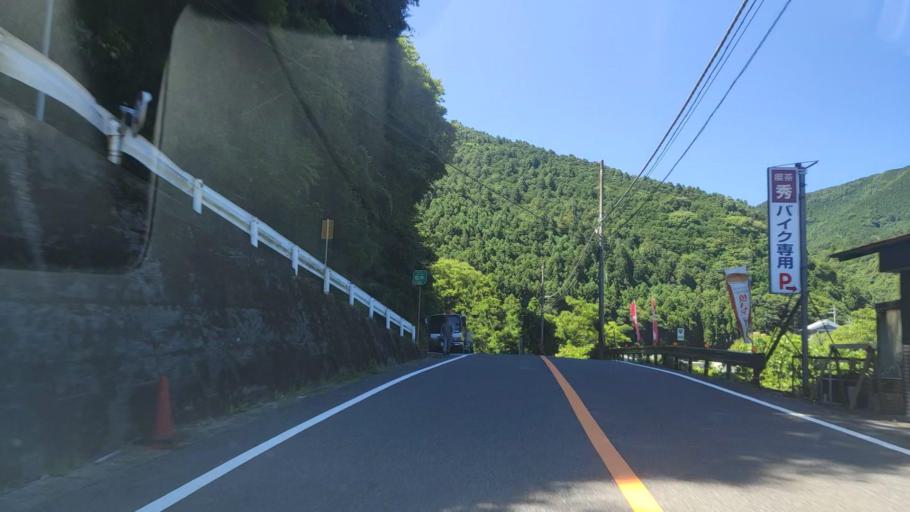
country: JP
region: Nara
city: Yoshino-cho
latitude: 34.2901
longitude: 135.9996
